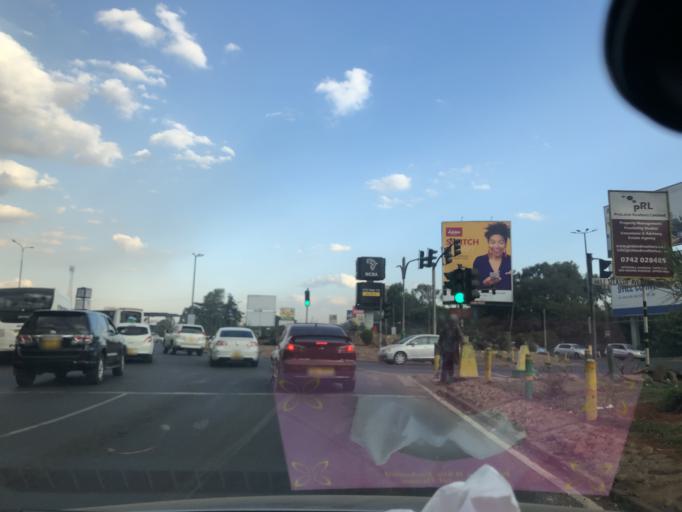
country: KE
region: Nairobi Area
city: Nairobi
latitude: -1.2924
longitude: 36.8203
